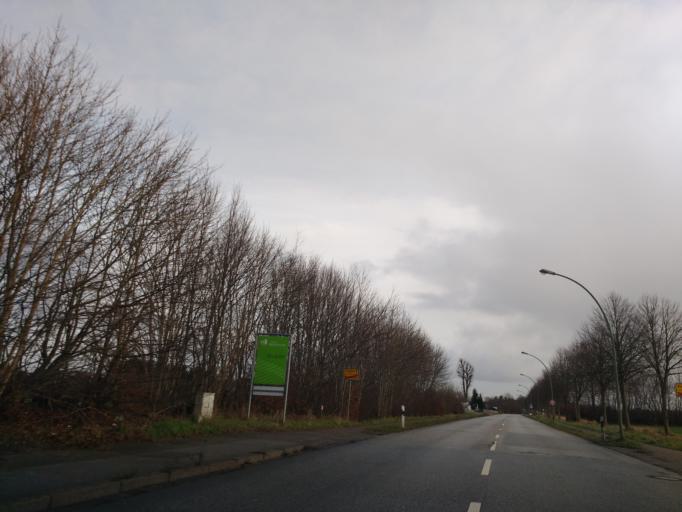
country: DE
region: Schleswig-Holstein
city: Tasdorf
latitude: 54.0731
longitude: 10.0188
